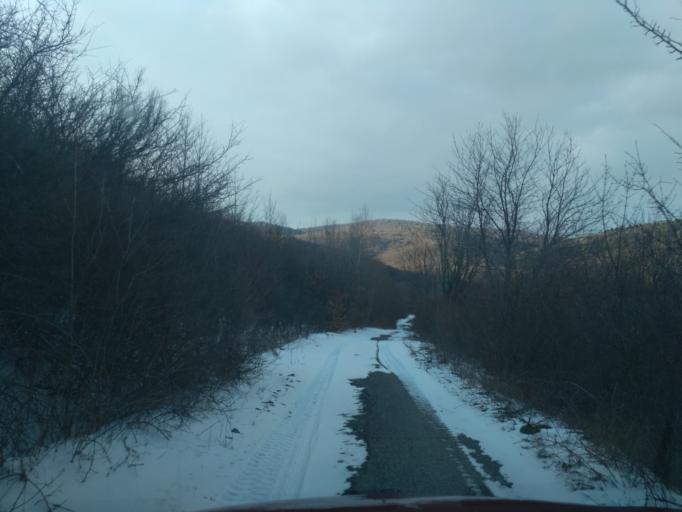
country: SK
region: Kosicky
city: Kosice
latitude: 48.7398
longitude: 21.1504
